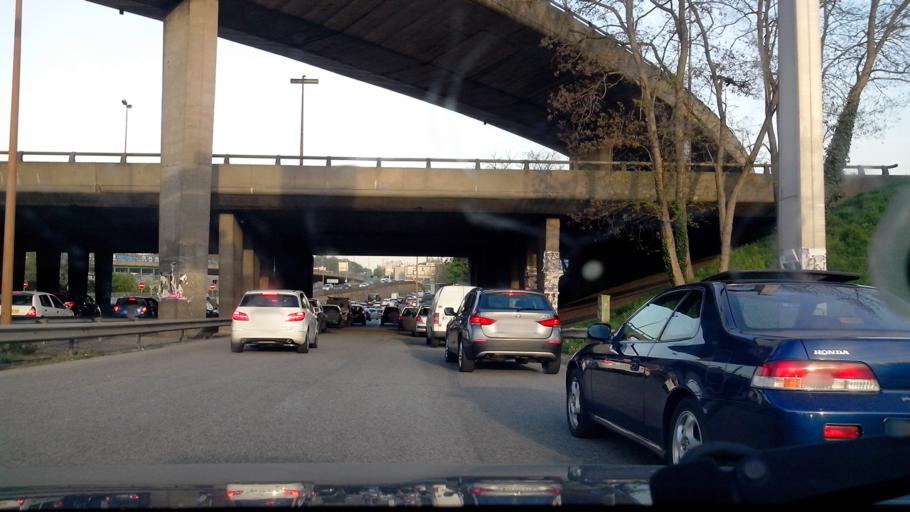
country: FR
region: Ile-de-France
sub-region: Departement de l'Essonne
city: Bievres
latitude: 48.7773
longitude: 2.2216
